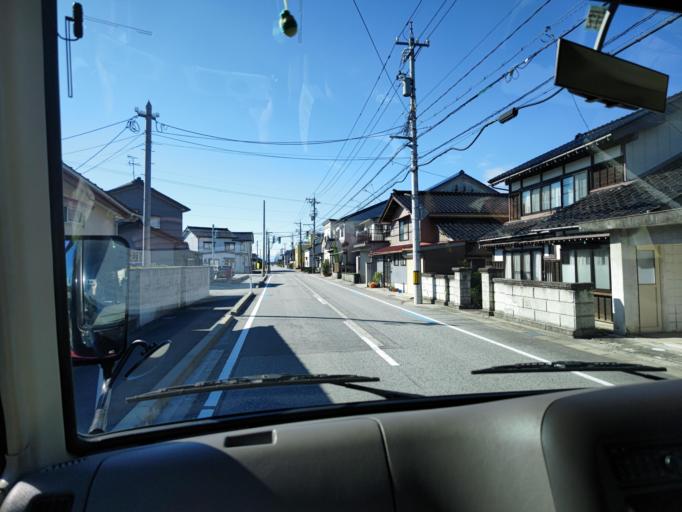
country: JP
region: Toyama
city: Nyuzen
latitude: 36.9063
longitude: 137.4258
